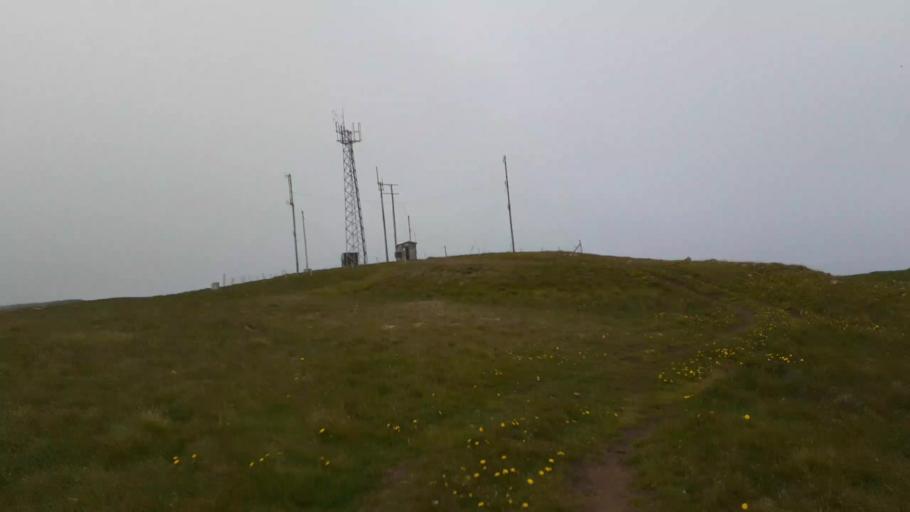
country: IS
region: Northeast
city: Dalvik
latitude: 66.5449
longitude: -17.9927
